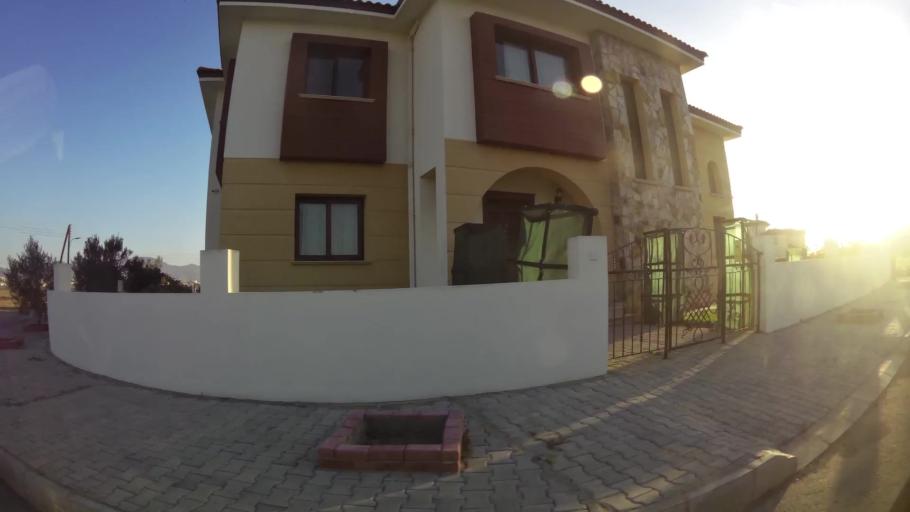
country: CY
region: Lefkosia
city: Nicosia
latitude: 35.1953
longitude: 33.3128
